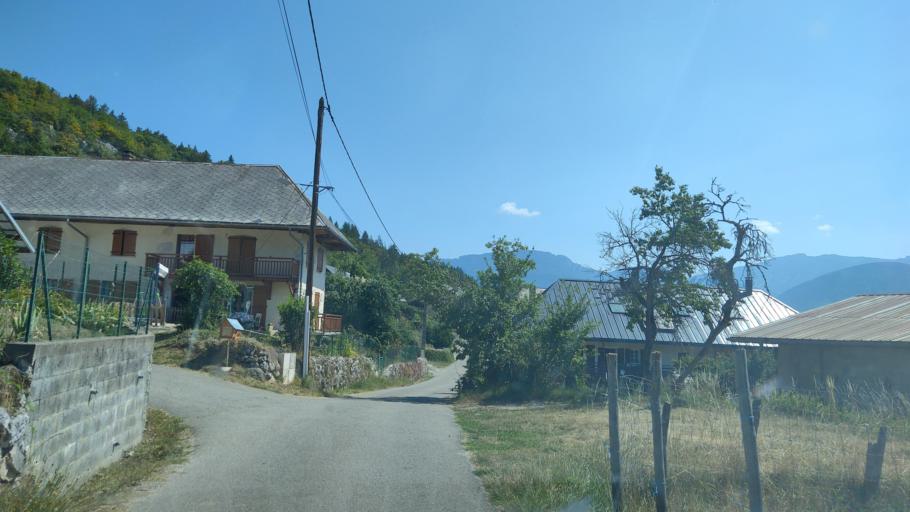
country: FR
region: Rhone-Alpes
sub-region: Departement de la Haute-Savoie
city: Cusy
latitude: 45.7201
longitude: 6.0743
